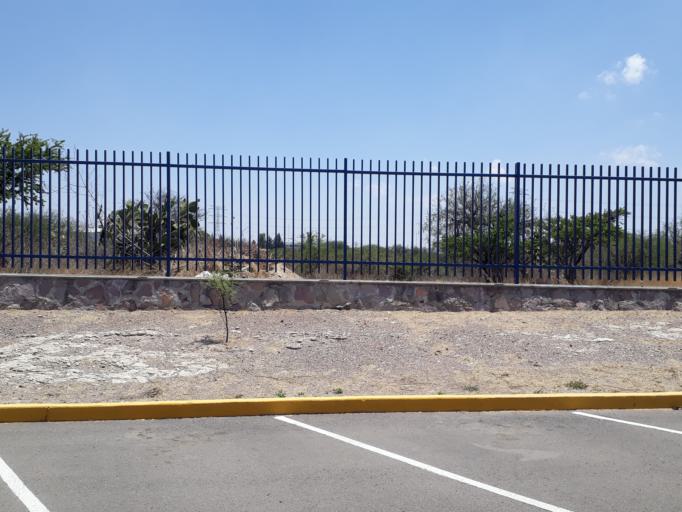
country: MX
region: Aguascalientes
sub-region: Aguascalientes
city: San Sebastian [Fraccionamiento]
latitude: 21.7941
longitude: -102.2913
